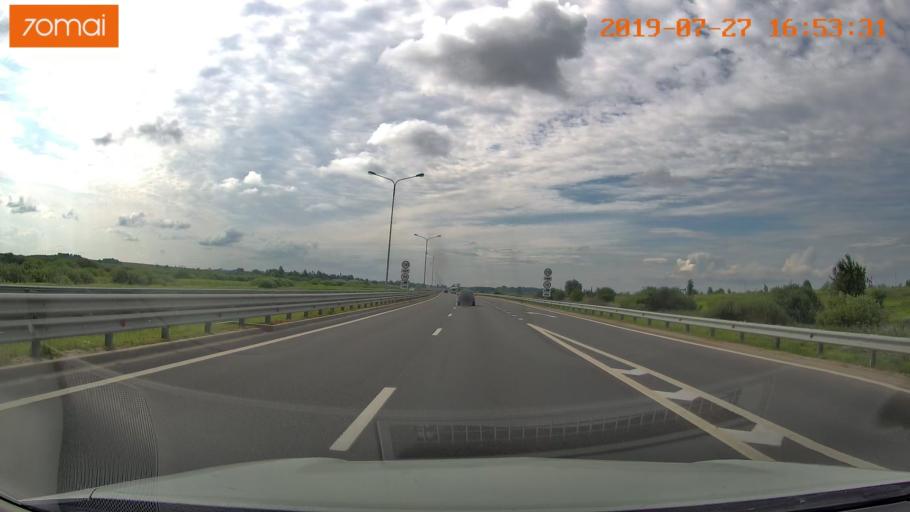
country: RU
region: Kaliningrad
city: Bol'shoe Isakovo
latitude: 54.6881
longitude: 20.8310
